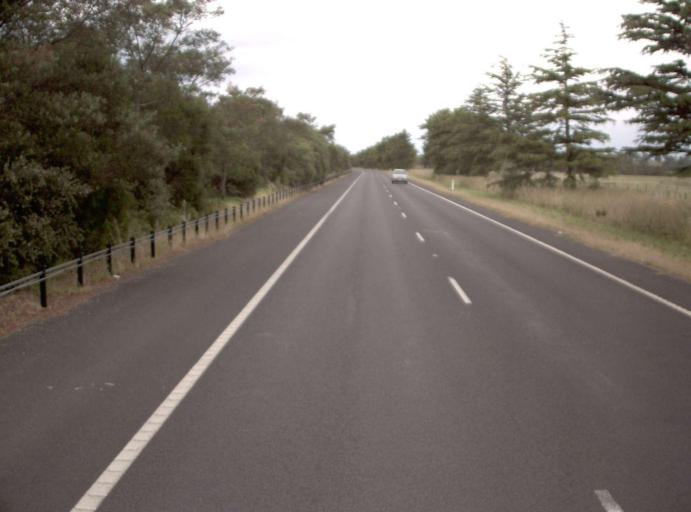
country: AU
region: Victoria
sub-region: East Gippsland
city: Bairnsdale
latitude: -37.8649
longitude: 147.6475
